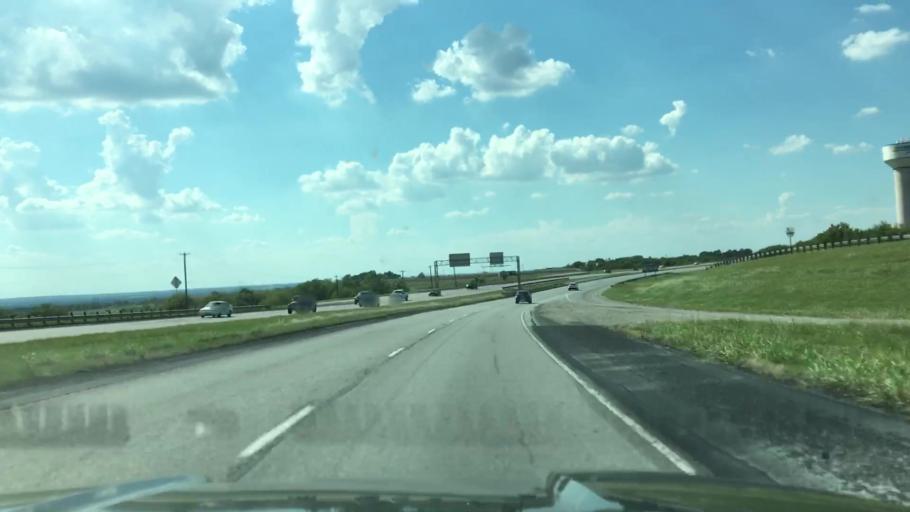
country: US
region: Texas
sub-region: Wise County
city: Rhome
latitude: 33.0471
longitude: -97.4742
